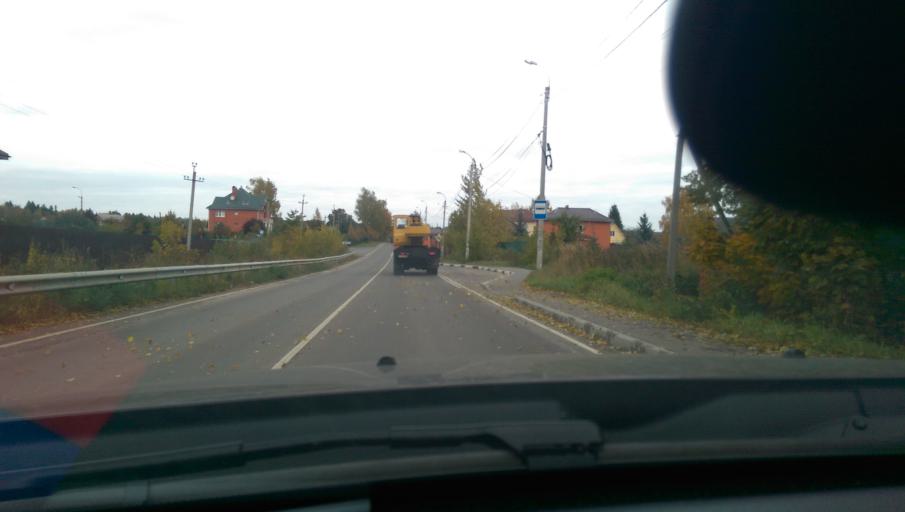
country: RU
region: Moskovskaya
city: Pirogovskiy
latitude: 56.0140
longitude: 37.7192
